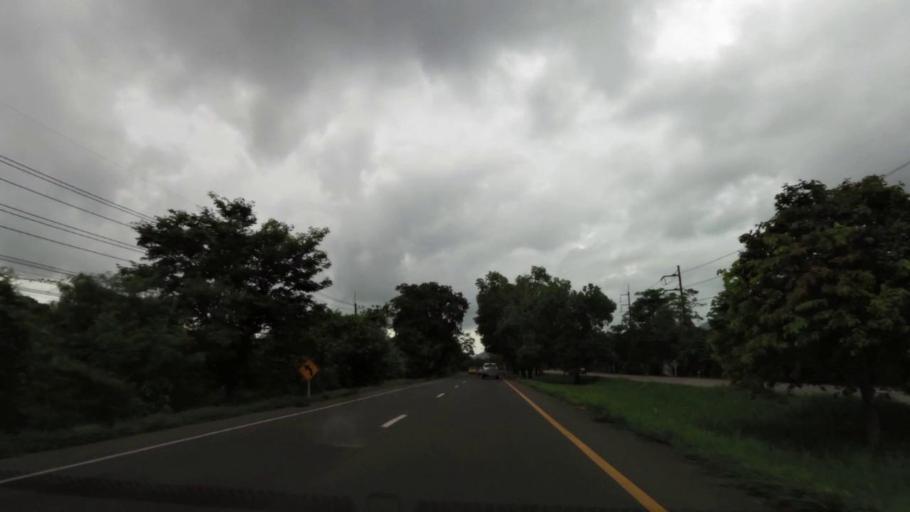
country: TH
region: Chanthaburi
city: Tha Mai
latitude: 12.6785
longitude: 102.0054
